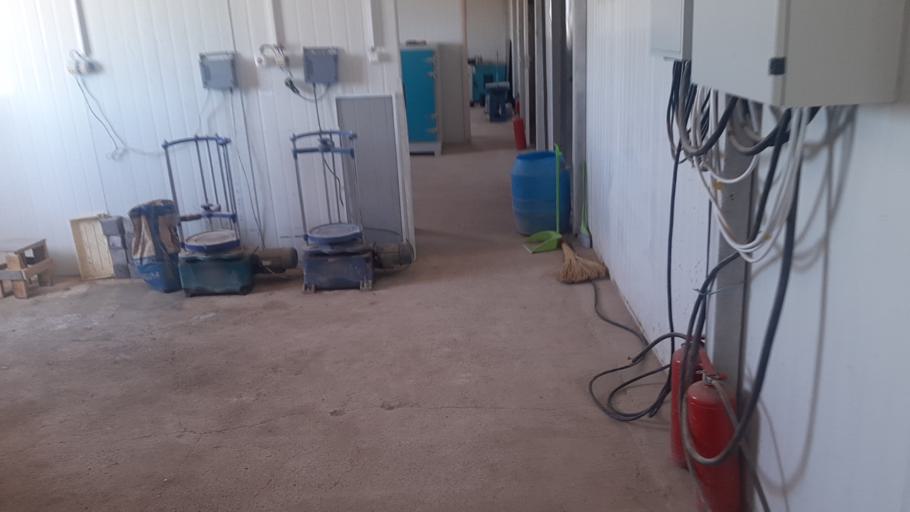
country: KZ
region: Qaraghandy
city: Balqash
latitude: 46.6459
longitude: 74.3971
